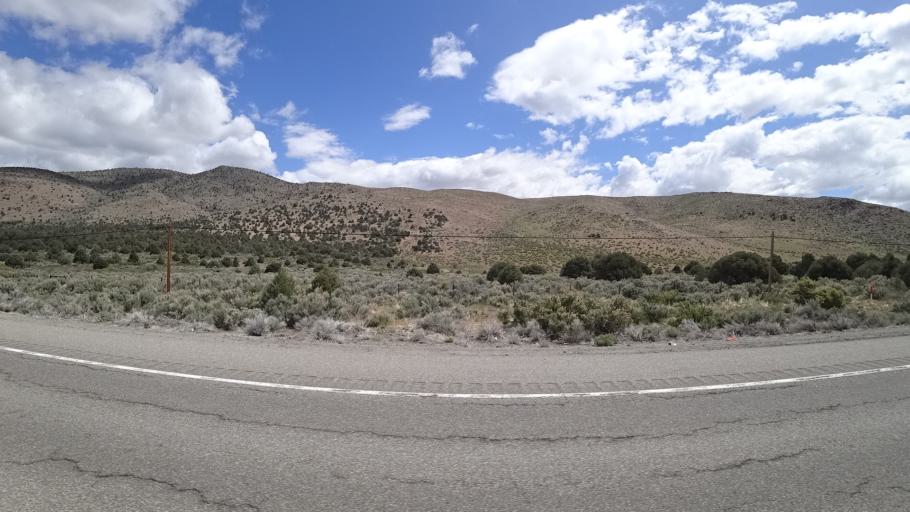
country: US
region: Nevada
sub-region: Lyon County
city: Smith Valley
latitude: 38.7448
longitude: -119.5654
